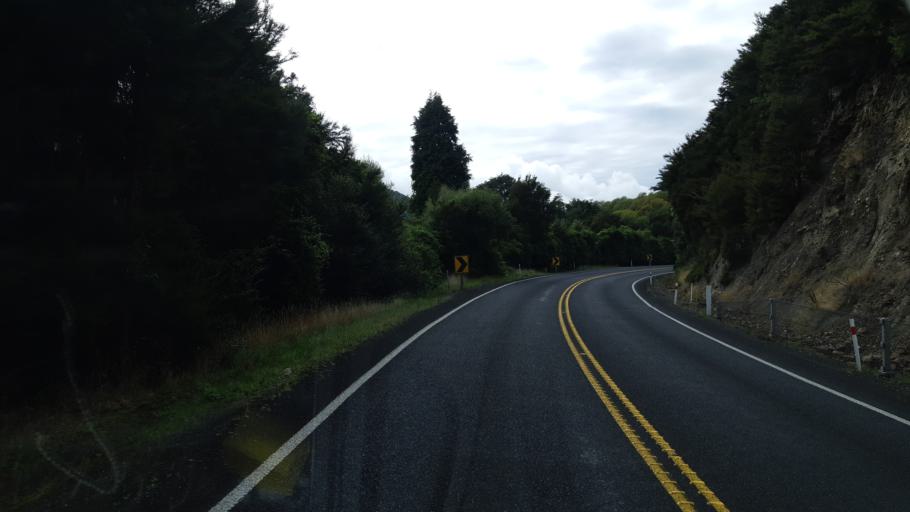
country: NZ
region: West Coast
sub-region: Buller District
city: Westport
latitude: -41.7812
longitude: 172.2711
